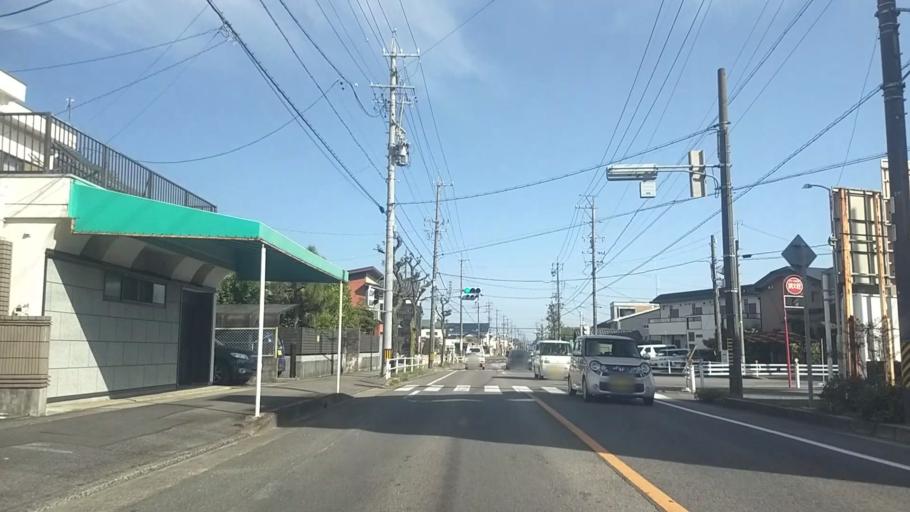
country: JP
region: Aichi
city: Anjo
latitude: 34.9514
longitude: 137.0940
